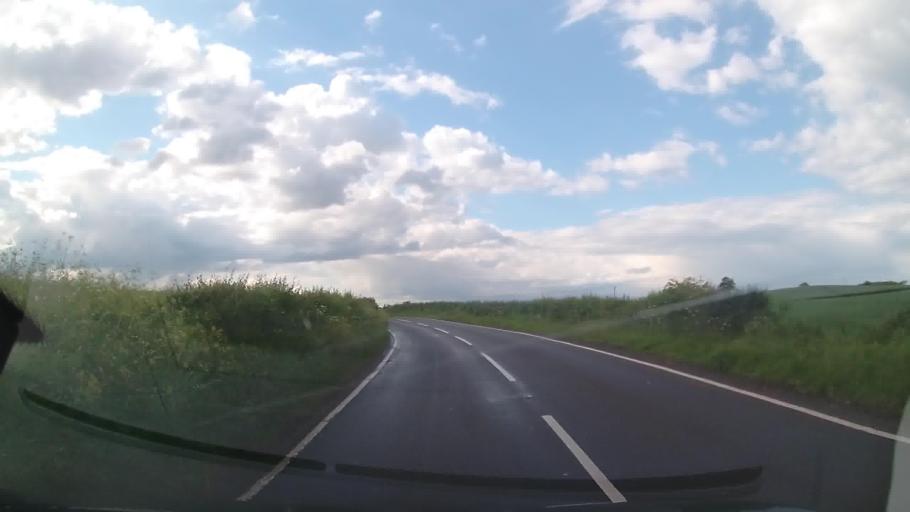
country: GB
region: England
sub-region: Shropshire
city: Withington
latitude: 52.6656
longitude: -2.6267
